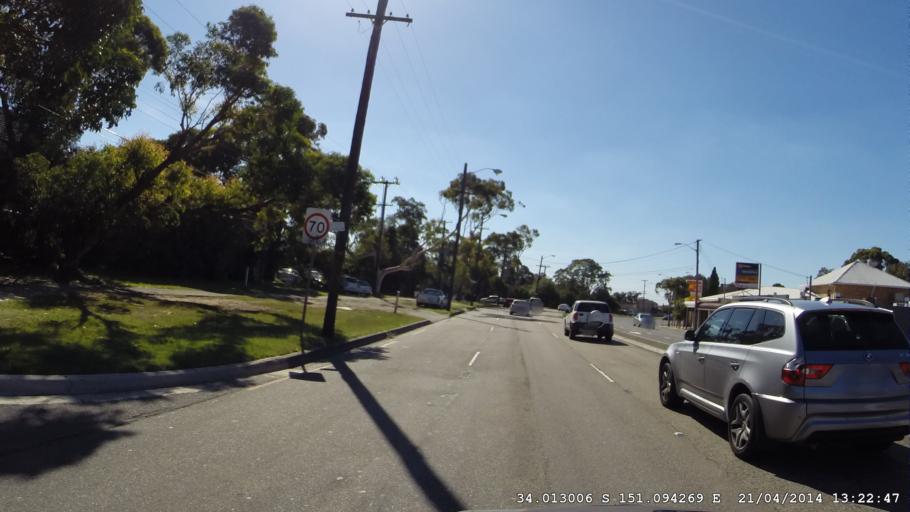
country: AU
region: New South Wales
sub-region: Sutherland Shire
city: Kareela
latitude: -34.0130
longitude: 151.0943
